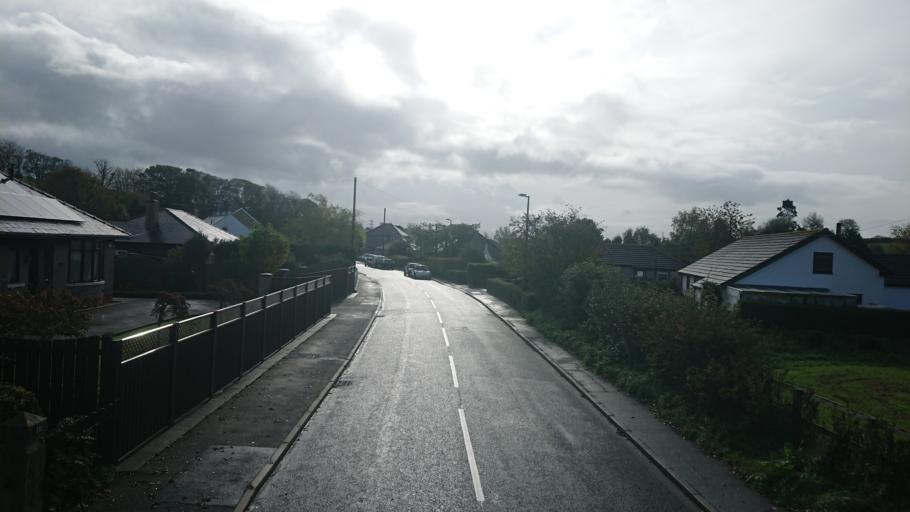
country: GB
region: England
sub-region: Lancashire
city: Bolton le Sands
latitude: 54.0791
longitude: -2.8037
